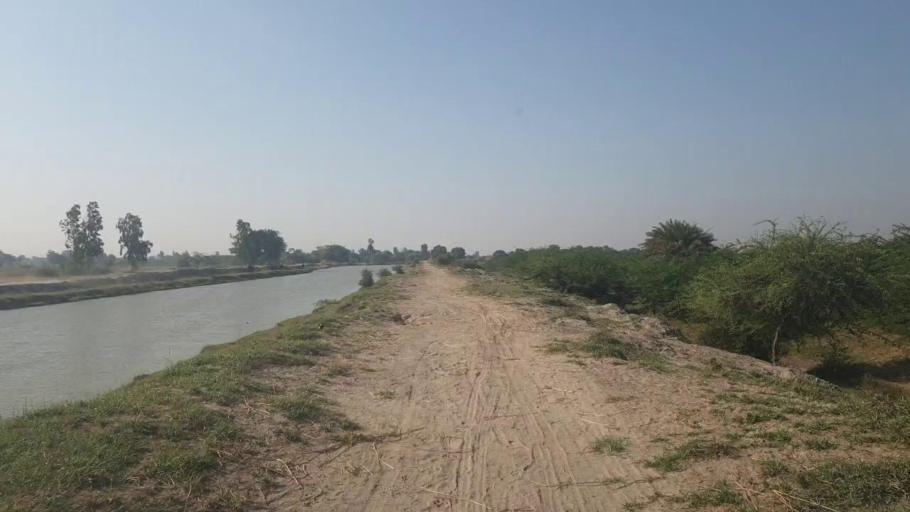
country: PK
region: Sindh
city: Badin
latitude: 24.6899
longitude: 68.8682
